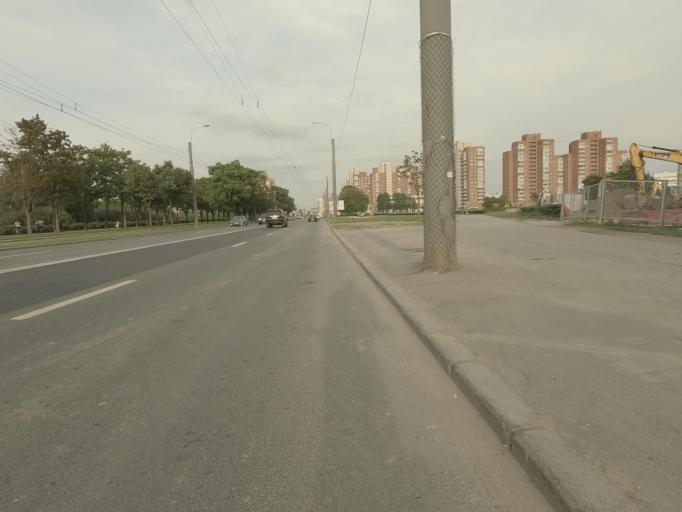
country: RU
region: St.-Petersburg
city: Uritsk
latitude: 59.8330
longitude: 30.1879
